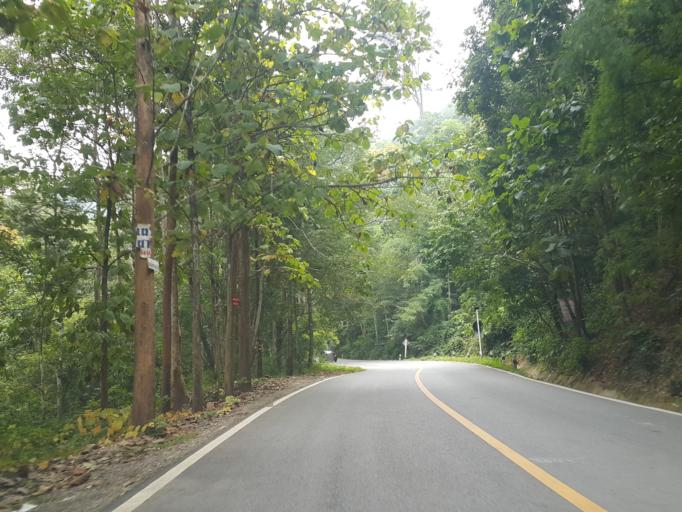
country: TH
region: Mae Hong Son
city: Mae Hi
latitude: 19.2752
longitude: 98.4987
